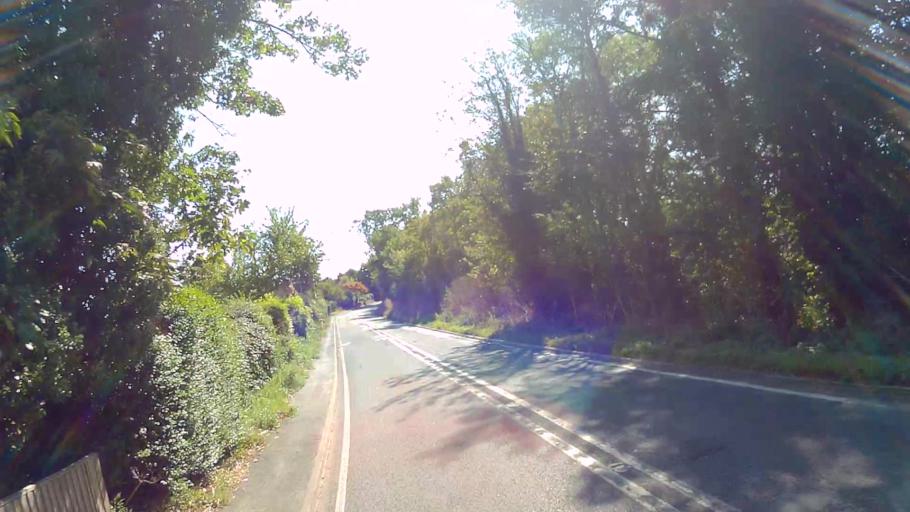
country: GB
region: England
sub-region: Wokingham
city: Swallowfield
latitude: 51.3816
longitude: -0.9651
